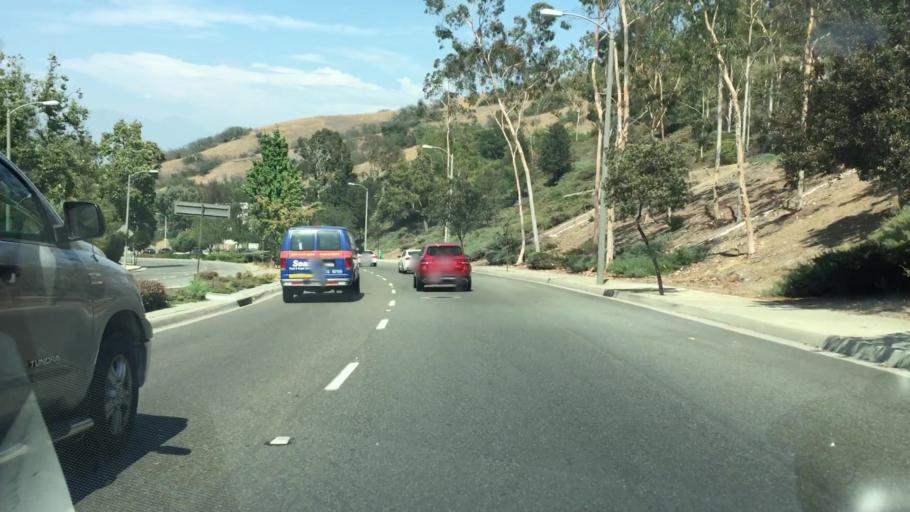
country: US
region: California
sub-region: Los Angeles County
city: Rowland Heights
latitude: 33.9601
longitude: -117.9164
